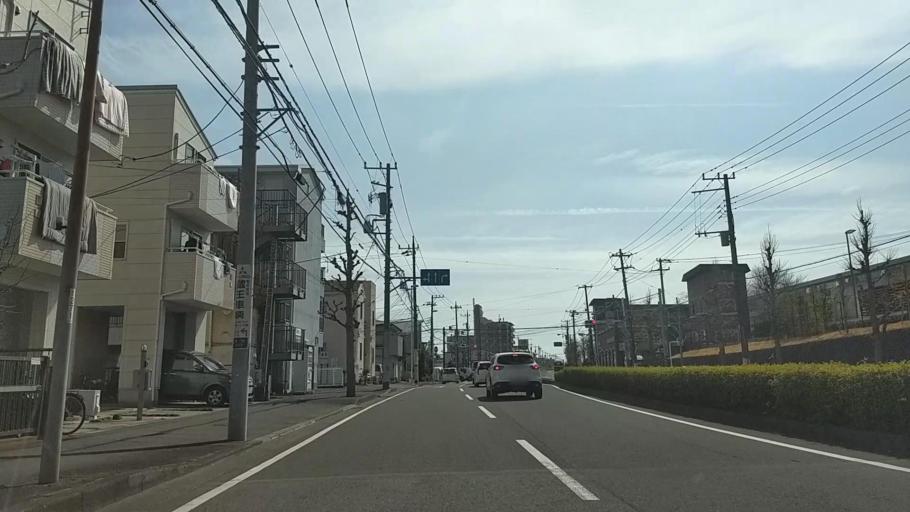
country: JP
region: Kanagawa
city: Fujisawa
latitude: 35.3946
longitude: 139.4577
